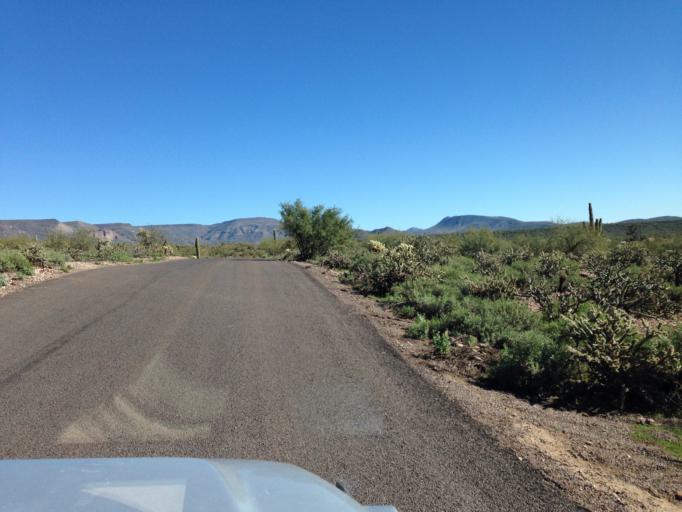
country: US
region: Arizona
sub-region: Maricopa County
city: New River
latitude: 33.9269
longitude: -112.0947
